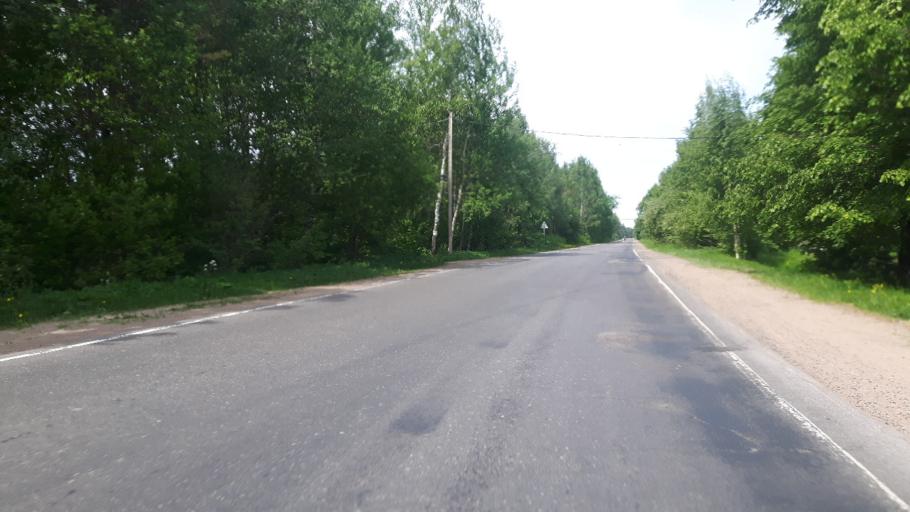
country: RU
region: Leningrad
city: Ust'-Luga
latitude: 59.6402
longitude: 28.2779
